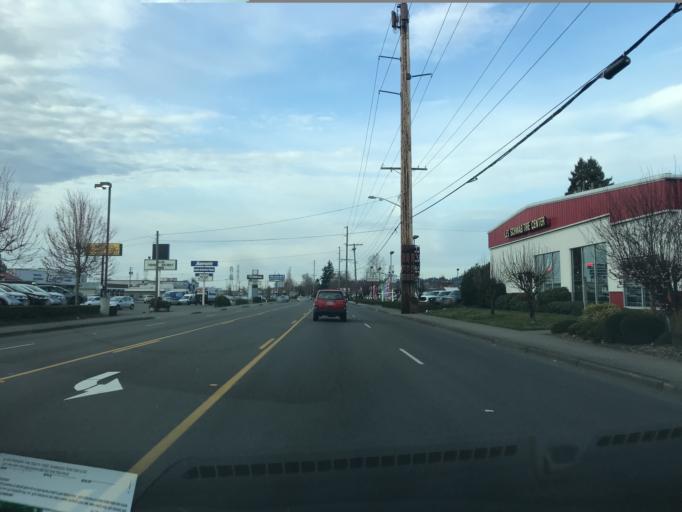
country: US
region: Washington
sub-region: King County
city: Auburn
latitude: 47.3303
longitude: -122.2215
